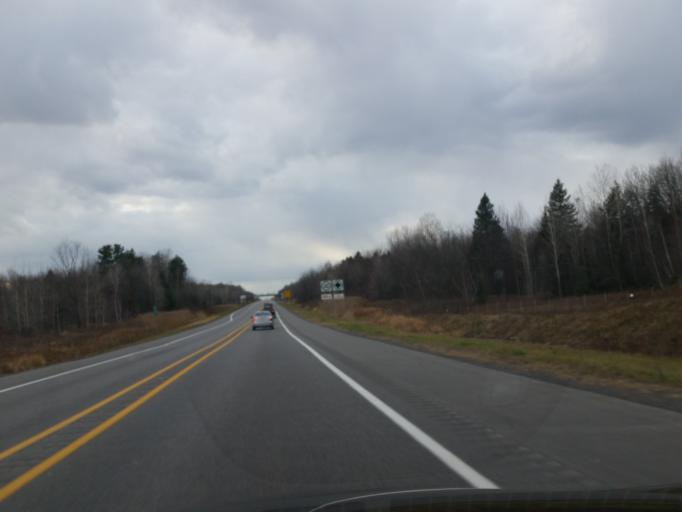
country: CA
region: Quebec
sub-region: Laurentides
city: Mirabel
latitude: 45.6836
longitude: -74.1182
